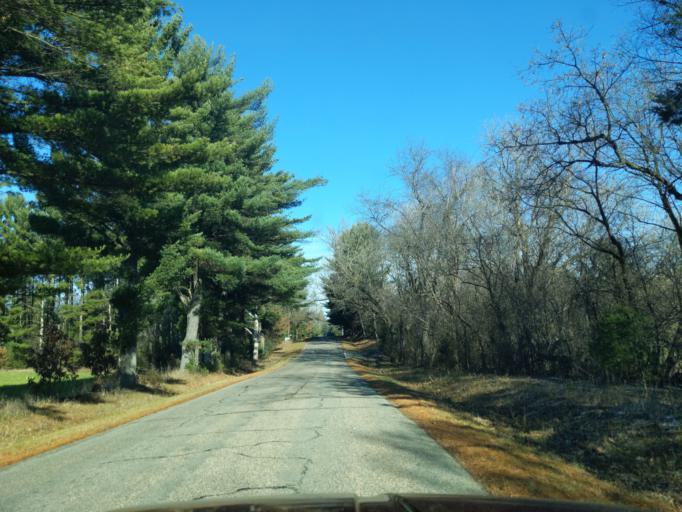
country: US
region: Wisconsin
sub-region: Waushara County
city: Silver Lake
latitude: 44.0791
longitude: -89.1939
